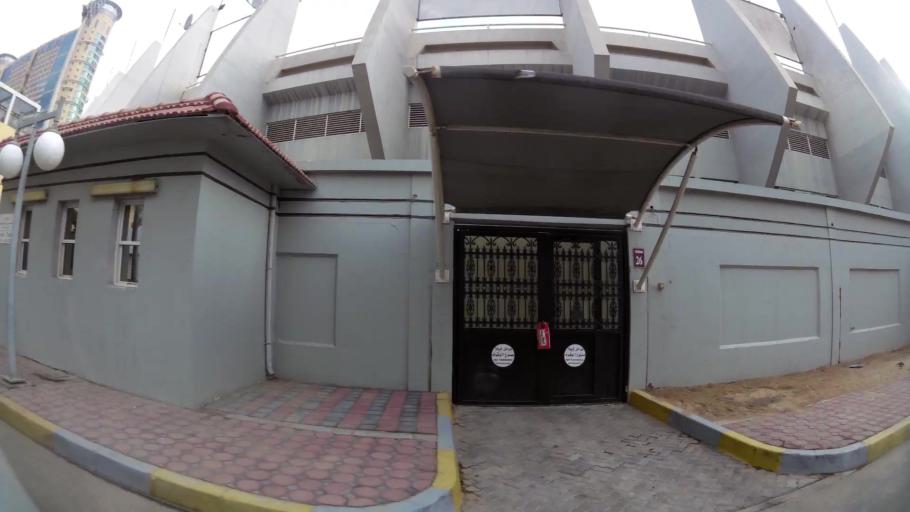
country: AE
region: Abu Dhabi
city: Abu Dhabi
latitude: 24.4686
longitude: 54.3745
